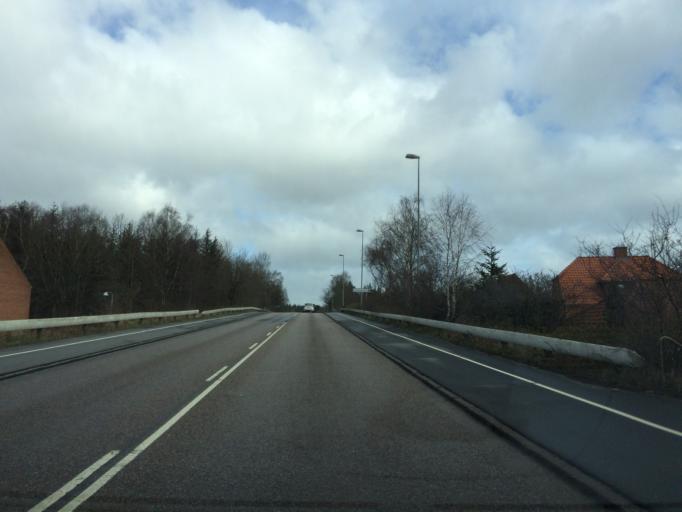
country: DK
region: Central Jutland
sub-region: Silkeborg Kommune
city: Silkeborg
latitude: 56.1617
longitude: 9.5297
